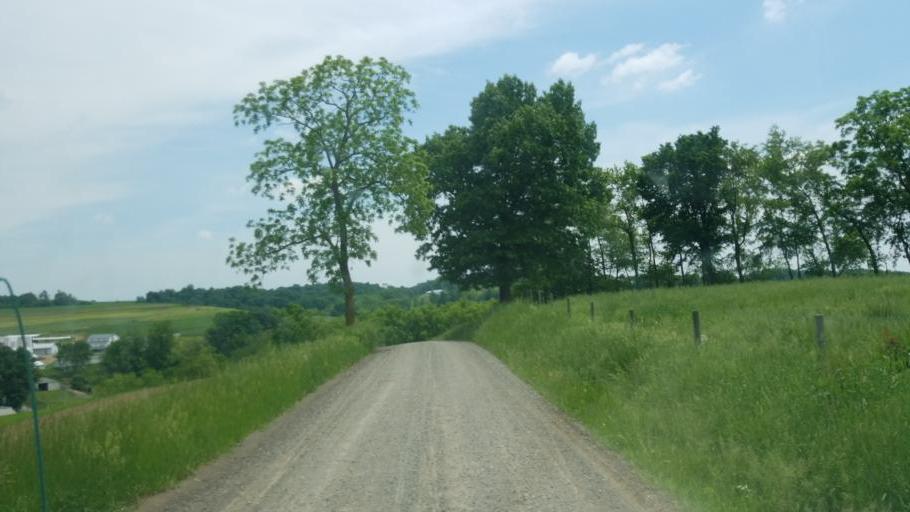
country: US
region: Ohio
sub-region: Holmes County
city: Millersburg
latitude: 40.4692
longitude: -81.7964
